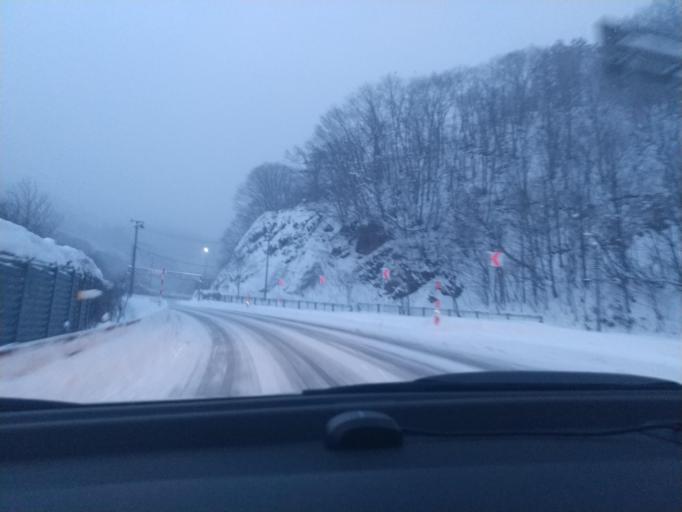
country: JP
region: Iwate
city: Shizukuishi
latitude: 39.7215
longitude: 140.8427
